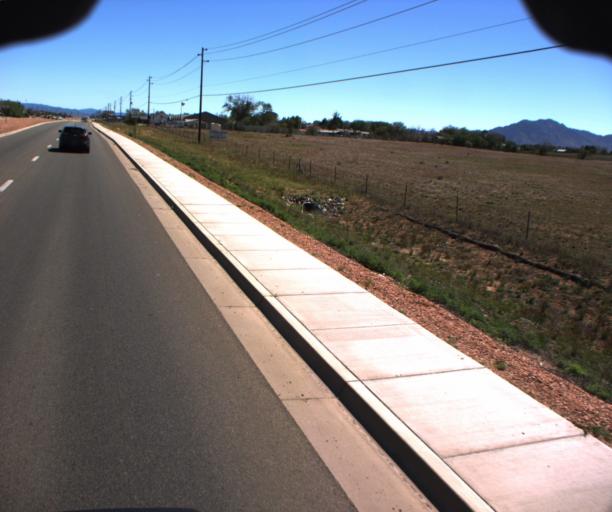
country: US
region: Arizona
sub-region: Yavapai County
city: Chino Valley
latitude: 34.7379
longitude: -112.4545
